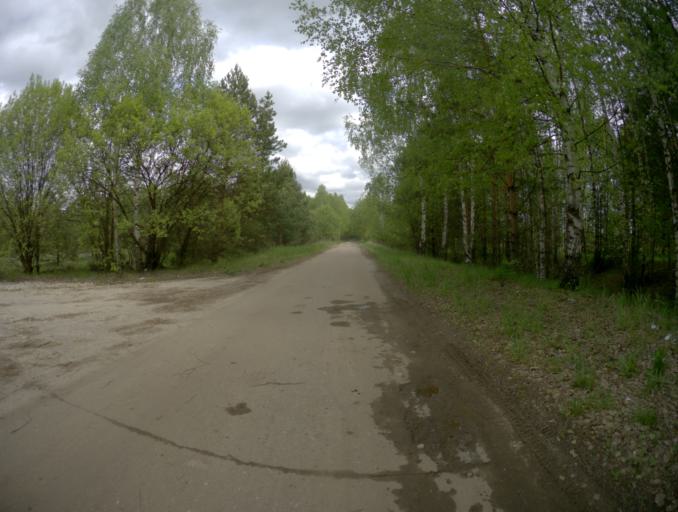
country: RU
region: Rjazan
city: Gus'-Zheleznyy
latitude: 55.1184
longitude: 40.9304
